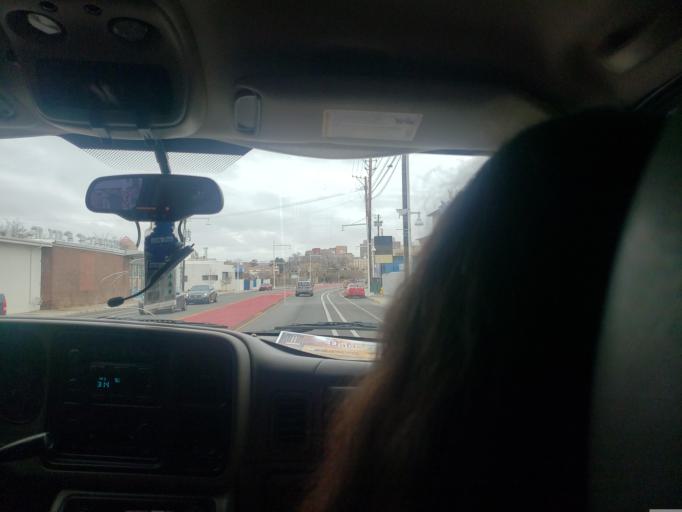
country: US
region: New Mexico
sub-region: Bernalillo County
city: Albuquerque
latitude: 35.0873
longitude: -106.6601
